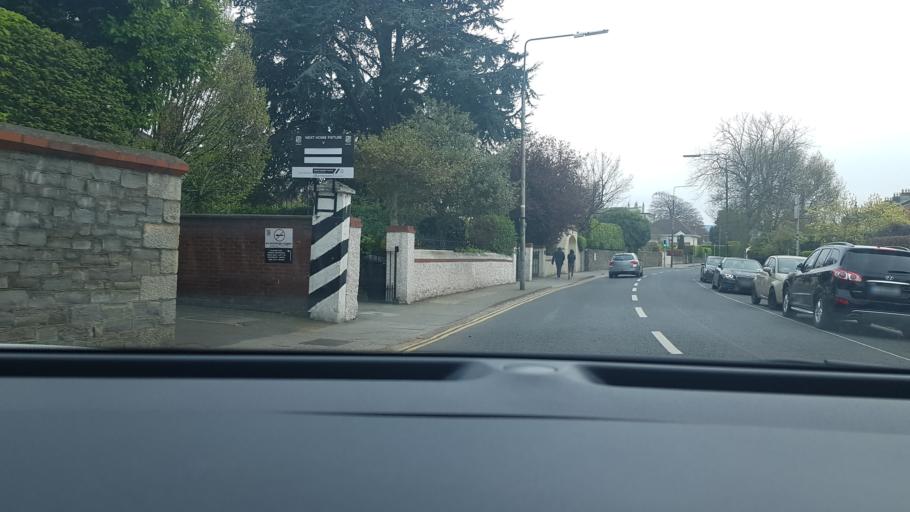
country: IE
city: Clonskeagh
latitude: 53.3225
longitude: -6.2301
